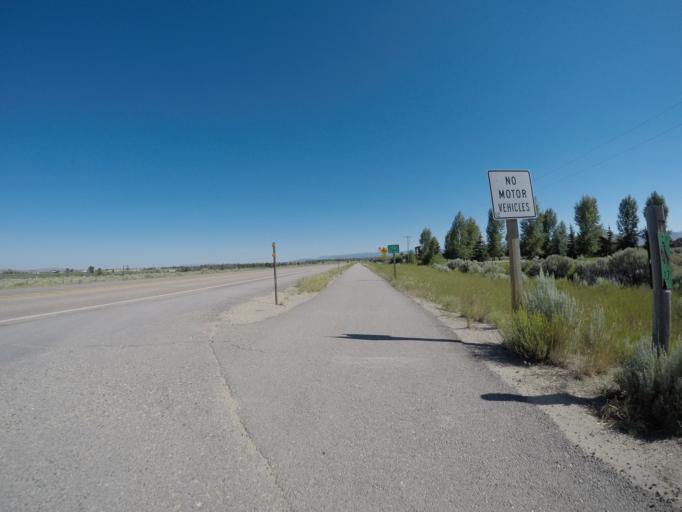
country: US
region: Wyoming
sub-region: Sublette County
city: Pinedale
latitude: 42.8390
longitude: -109.8466
